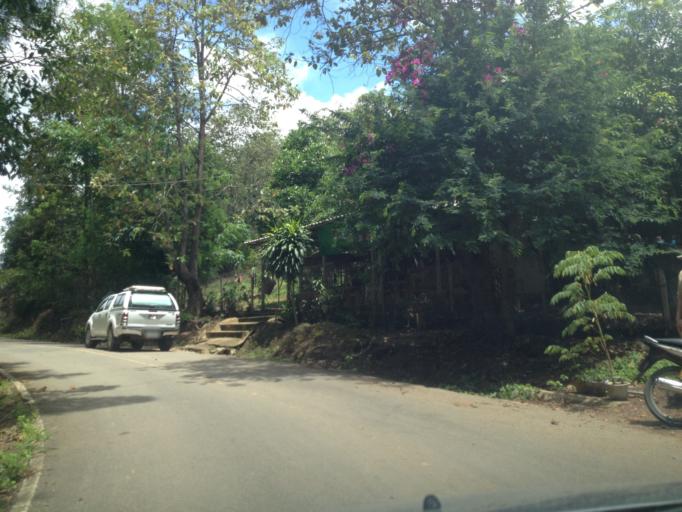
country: TH
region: Chiang Mai
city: Hang Dong
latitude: 18.7133
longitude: 98.8972
